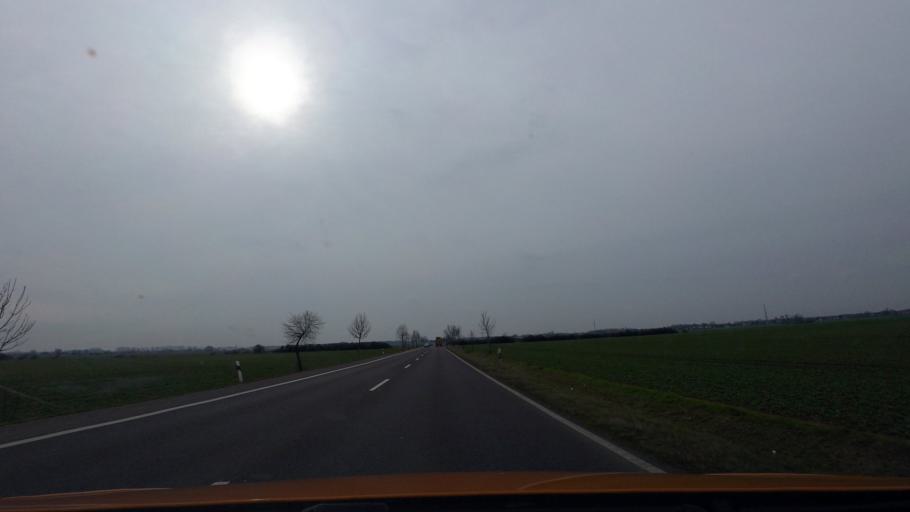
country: DE
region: Saxony-Anhalt
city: Gerwisch
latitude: 52.1660
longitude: 11.7416
